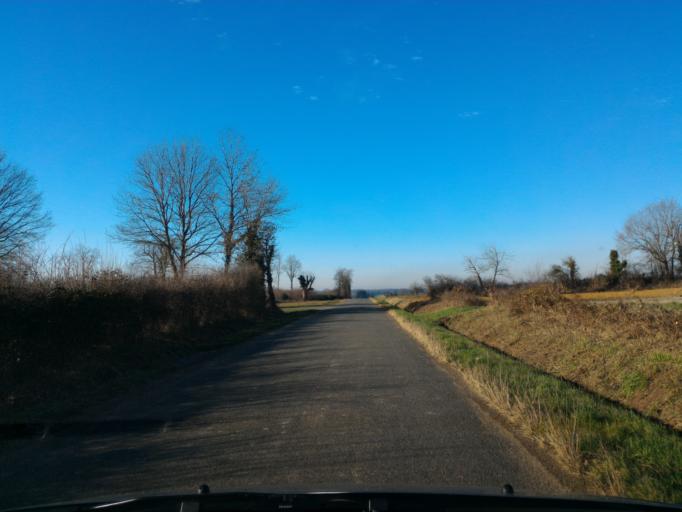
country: FR
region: Poitou-Charentes
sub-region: Departement de la Charente
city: Nanteuil-en-Vallee
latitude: 45.9556
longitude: 0.3468
